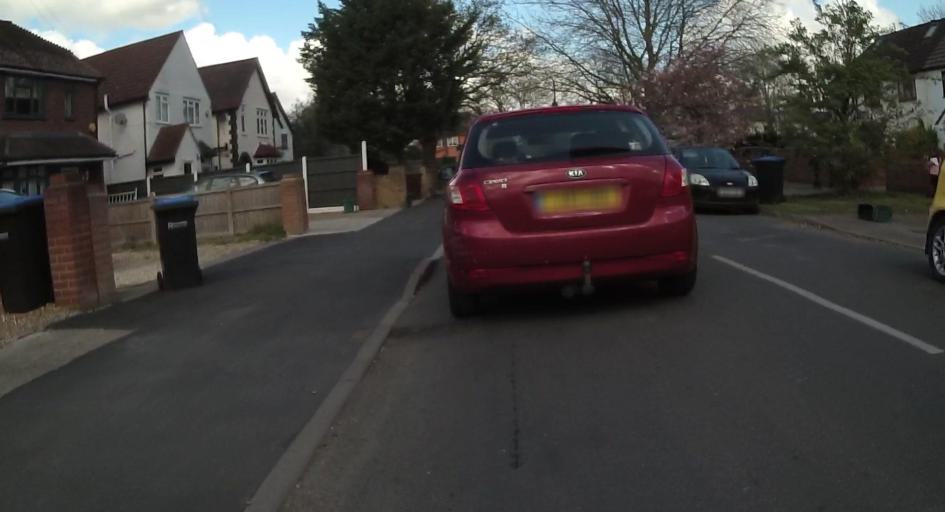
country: GB
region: England
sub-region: Surrey
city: Addlestone
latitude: 51.3750
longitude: -0.5015
